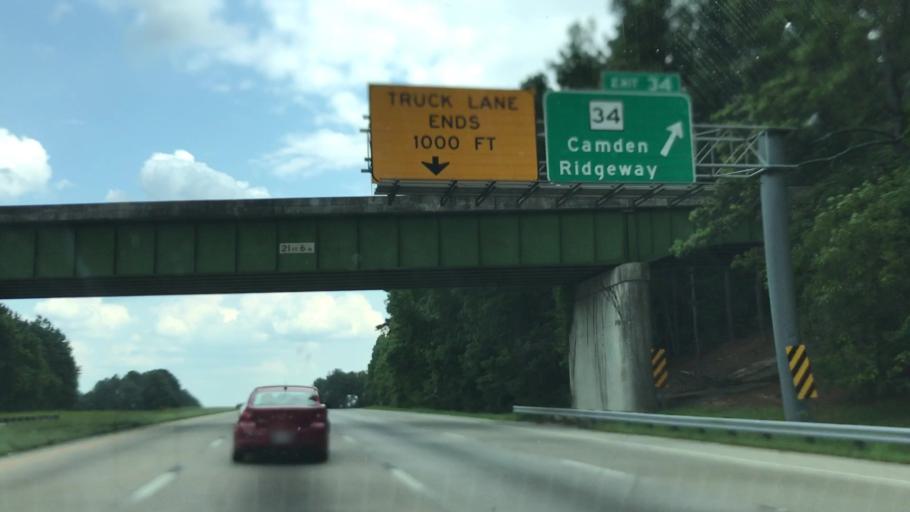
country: US
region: South Carolina
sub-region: Fairfield County
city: Winnsboro Mills
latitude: 34.3131
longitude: -81.0029
